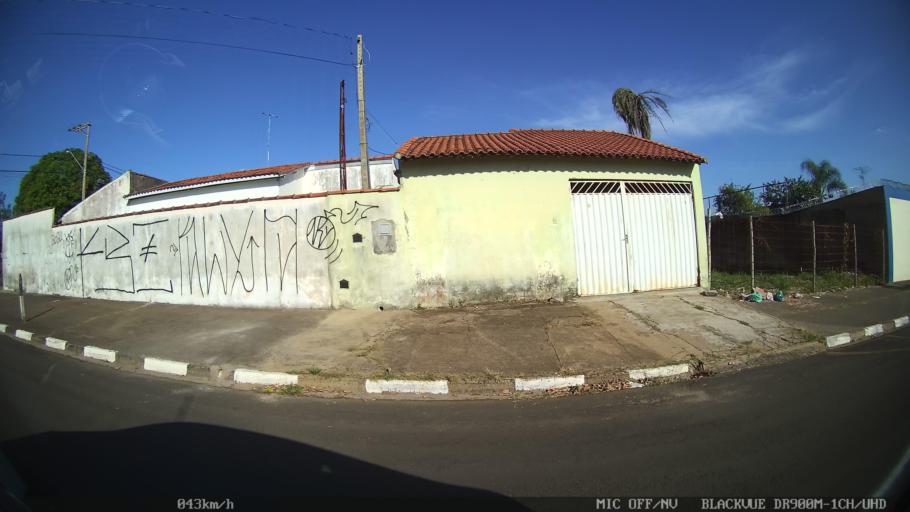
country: BR
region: Sao Paulo
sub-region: Franca
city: Franca
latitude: -20.5147
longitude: -47.4117
